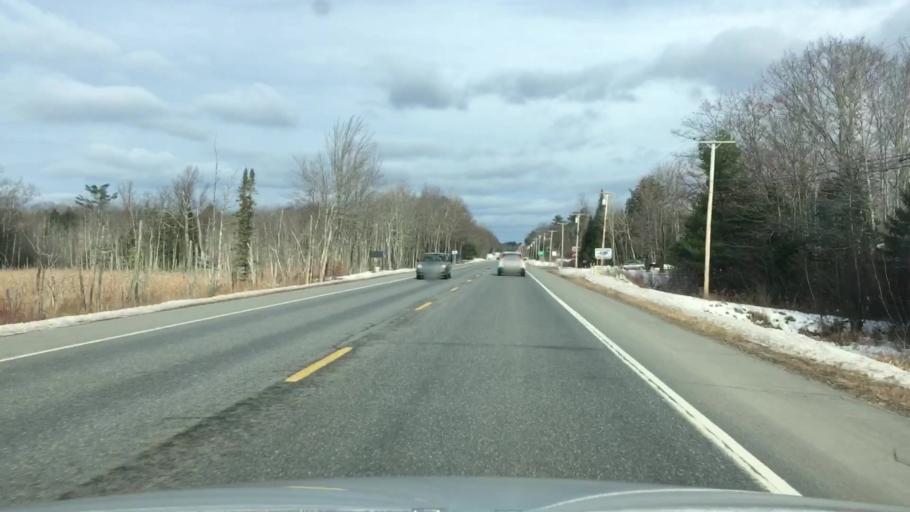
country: US
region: Maine
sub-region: Kennebec County
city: Winthrop
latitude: 44.2771
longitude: -70.0070
